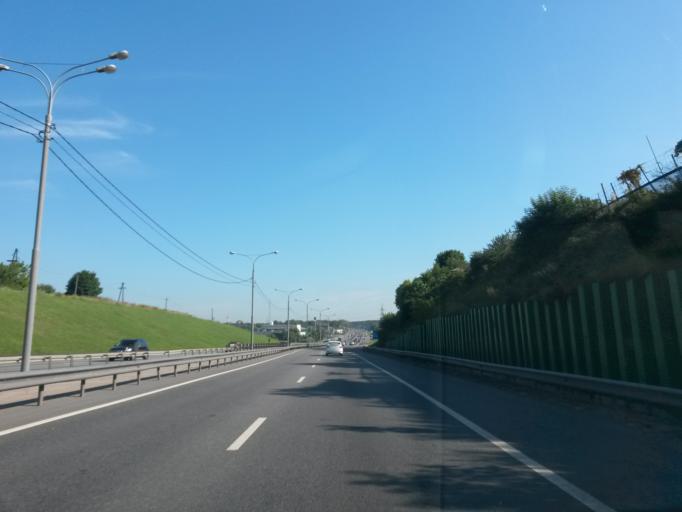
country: RU
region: Moskovskaya
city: Lesnyye Polyany
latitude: 55.9873
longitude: 37.8719
